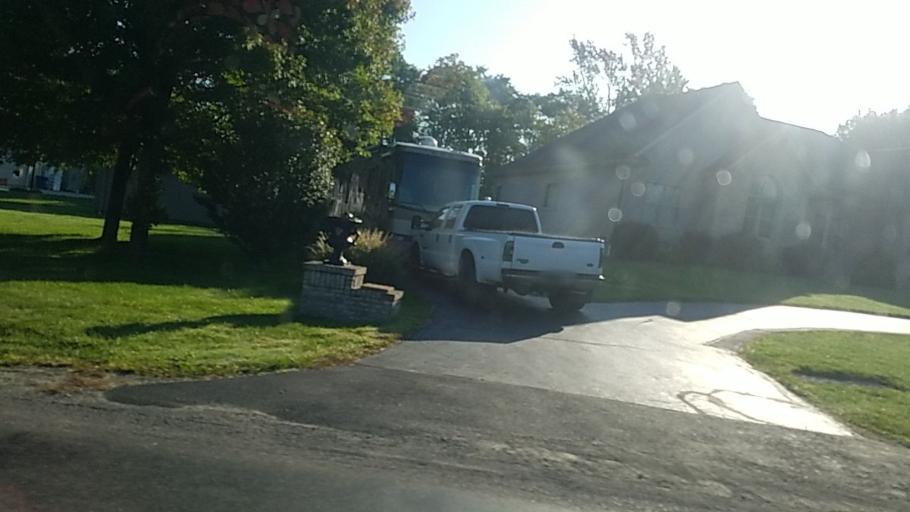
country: US
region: Ohio
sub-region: Trumbull County
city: Niles
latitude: 41.1606
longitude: -80.7535
